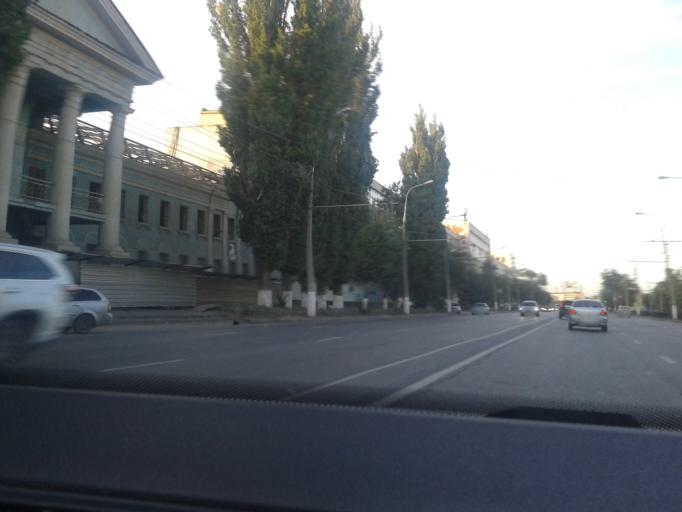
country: RU
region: Volgograd
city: Volgograd
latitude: 48.7316
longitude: 44.5410
